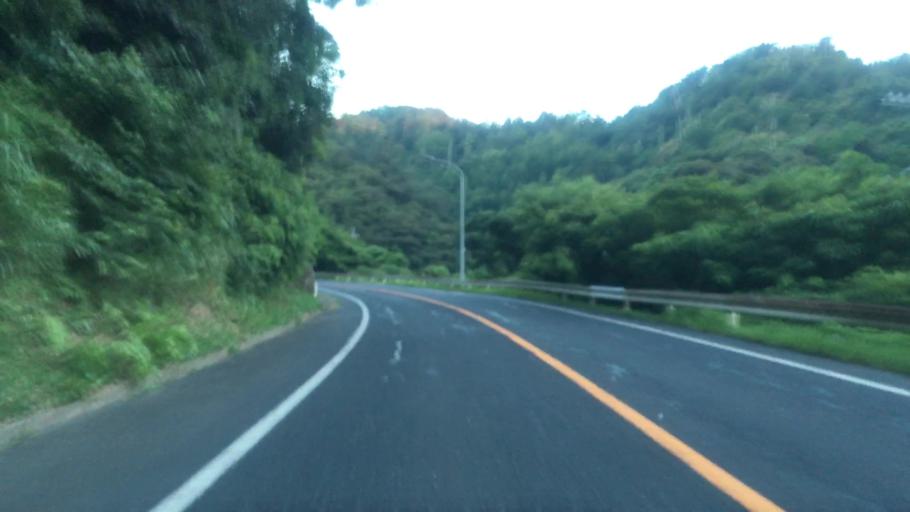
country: JP
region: Tottori
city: Tottori
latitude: 35.5970
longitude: 134.3517
